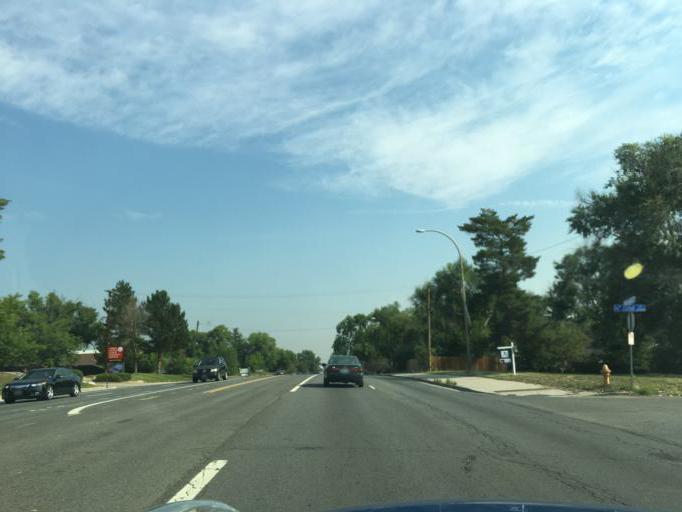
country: US
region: Colorado
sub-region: Jefferson County
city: Wheat Ridge
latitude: 39.7495
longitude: -105.0814
